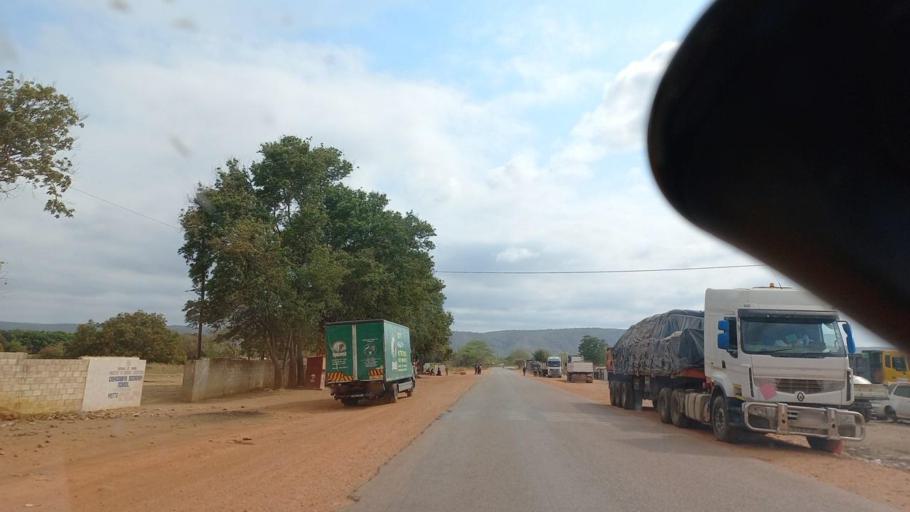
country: ZM
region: Lusaka
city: Chongwe
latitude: -15.0822
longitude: 29.5760
